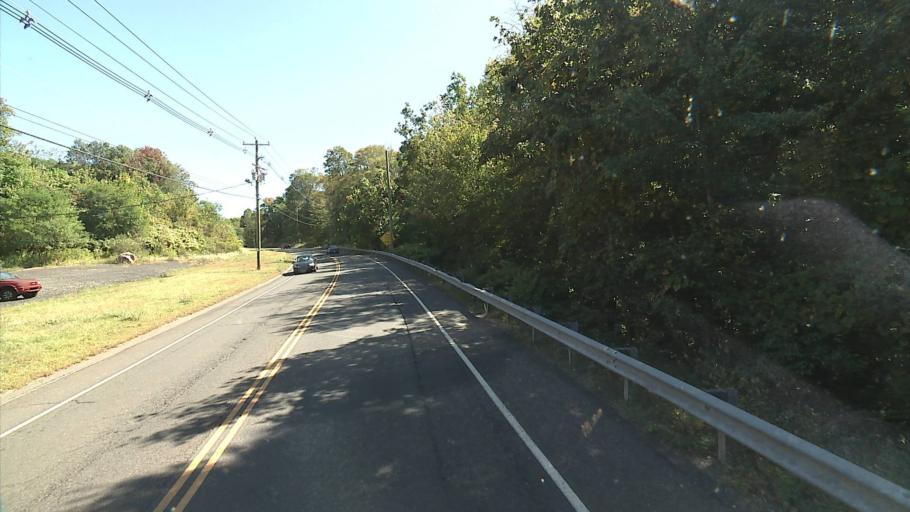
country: US
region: Connecticut
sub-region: New Haven County
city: Naugatuck
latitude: 41.5052
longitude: -73.0260
